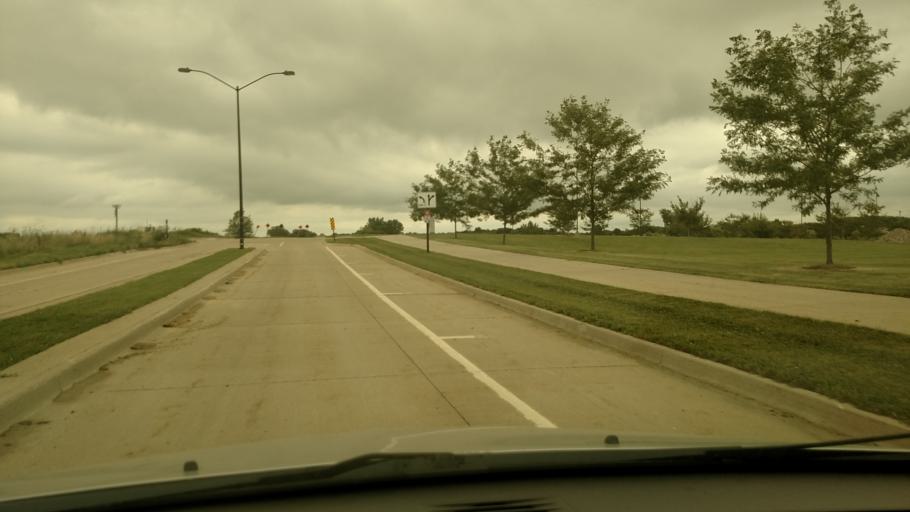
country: US
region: Iowa
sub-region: Polk County
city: Ankeny
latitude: 41.7122
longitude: -93.6114
